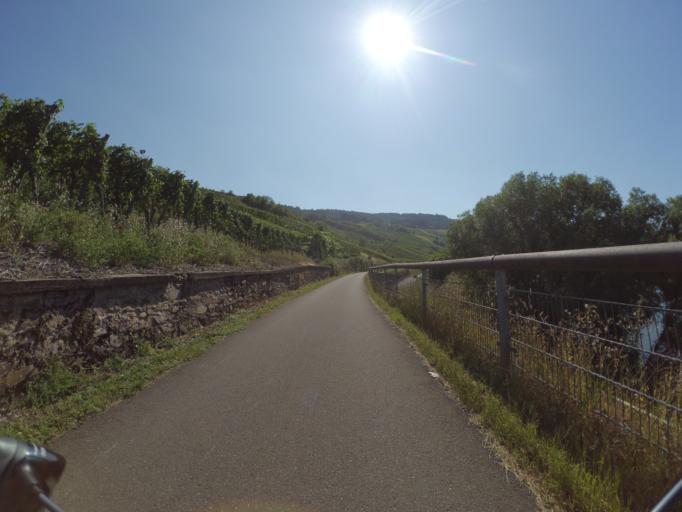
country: DE
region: Rheinland-Pfalz
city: Trittenheim
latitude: 49.8174
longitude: 6.9046
